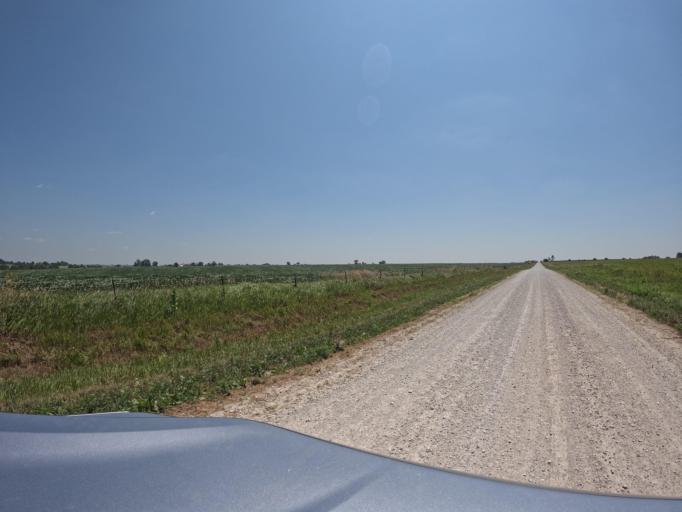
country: US
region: Iowa
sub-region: Keokuk County
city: Sigourney
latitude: 41.2728
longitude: -92.1807
